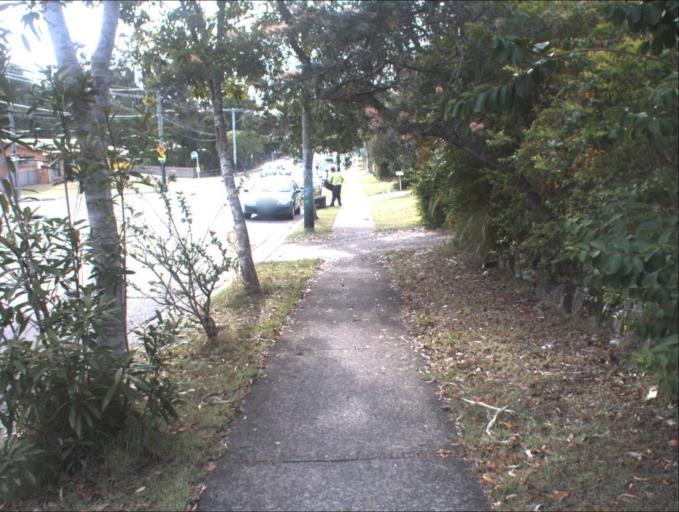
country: AU
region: Queensland
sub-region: Logan
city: Slacks Creek
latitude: -27.6408
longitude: 153.1587
